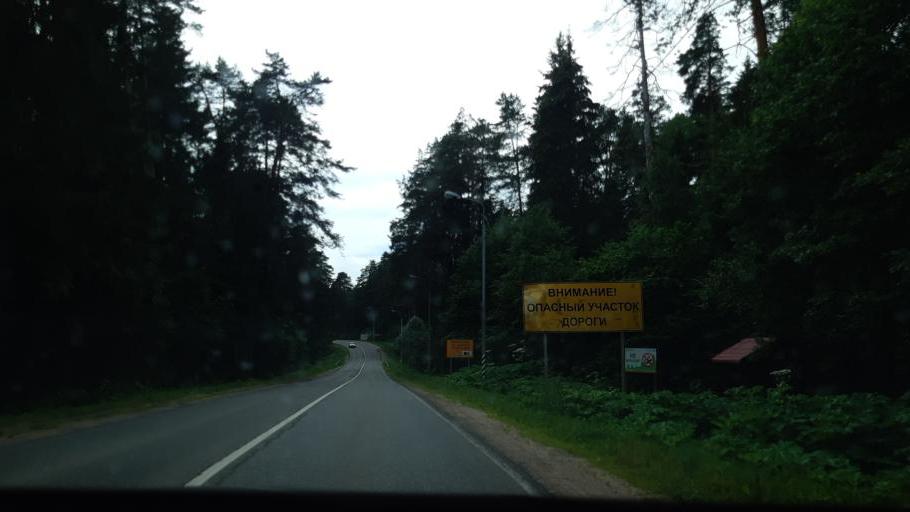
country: RU
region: Moskovskaya
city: Vereya
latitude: 55.3636
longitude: 36.2088
